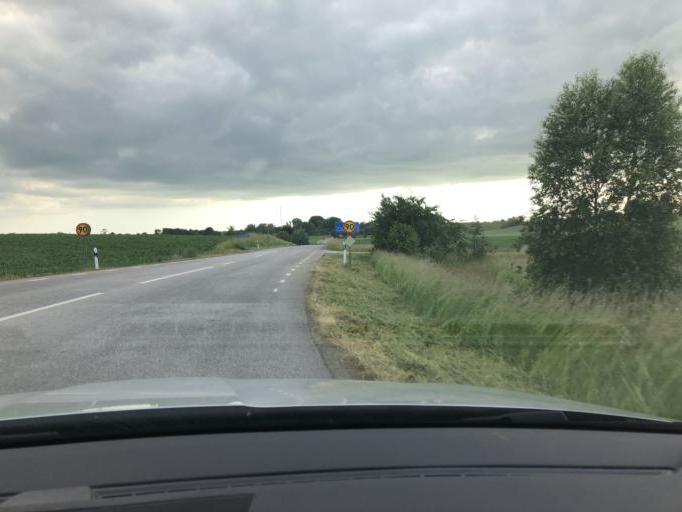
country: SE
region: Skane
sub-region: Simrishamns Kommun
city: Simrishamn
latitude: 55.5344
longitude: 14.2753
